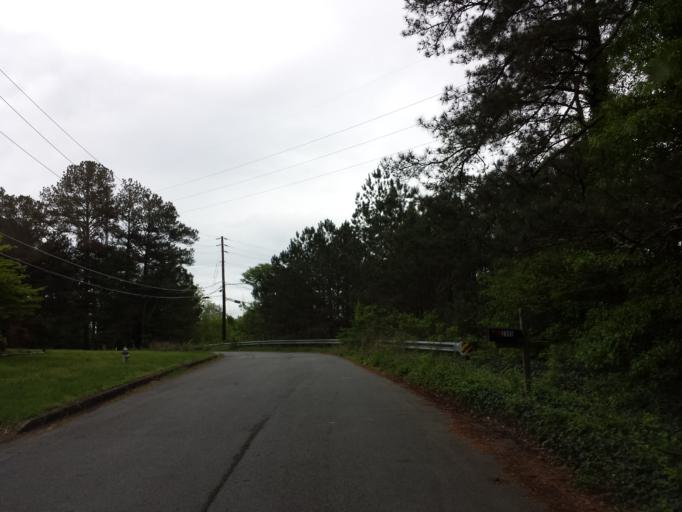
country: US
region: Georgia
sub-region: Cherokee County
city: Woodstock
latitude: 34.0243
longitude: -84.4843
